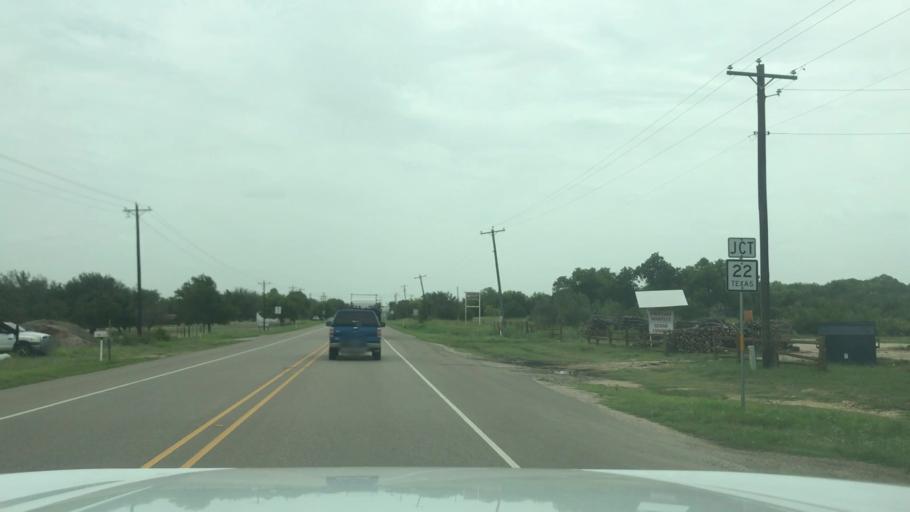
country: US
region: Texas
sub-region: Bosque County
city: Meridian
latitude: 31.9184
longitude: -97.6706
